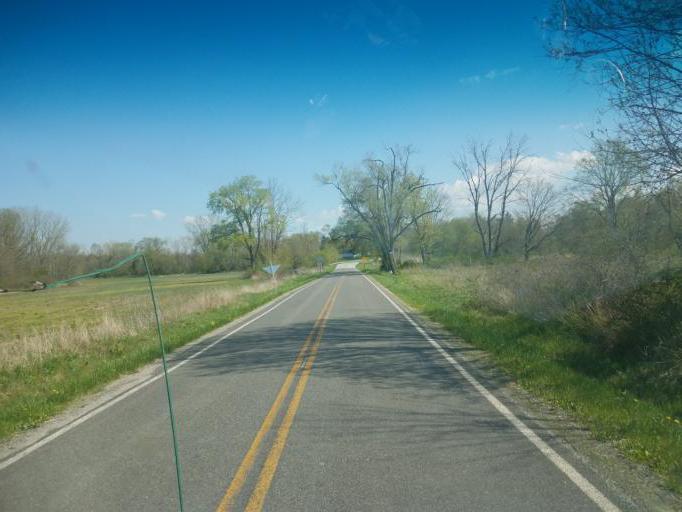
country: US
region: Ohio
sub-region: Medina County
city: Westfield Center
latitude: 40.9909
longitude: -81.9408
